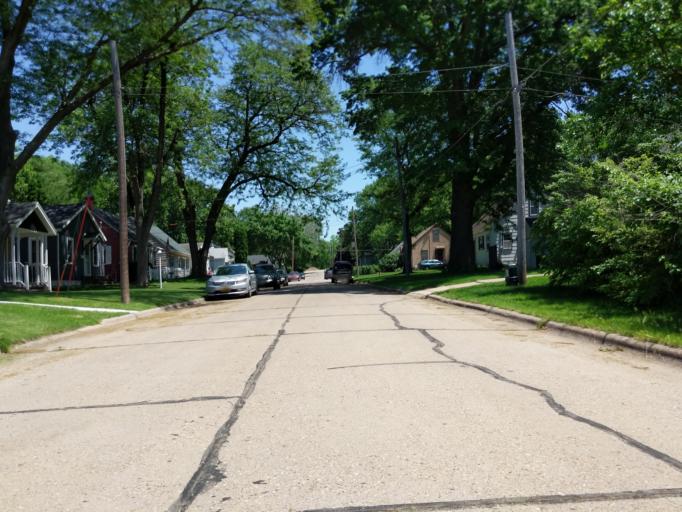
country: US
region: Iowa
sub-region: Linn County
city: Cedar Rapids
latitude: 42.0186
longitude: -91.6405
